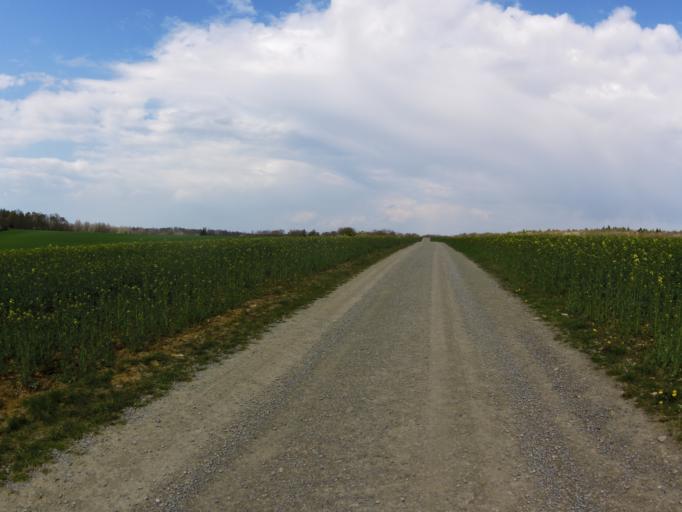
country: DE
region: Bavaria
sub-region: Regierungsbezirk Unterfranken
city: Rimpar
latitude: 49.8661
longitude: 9.9481
